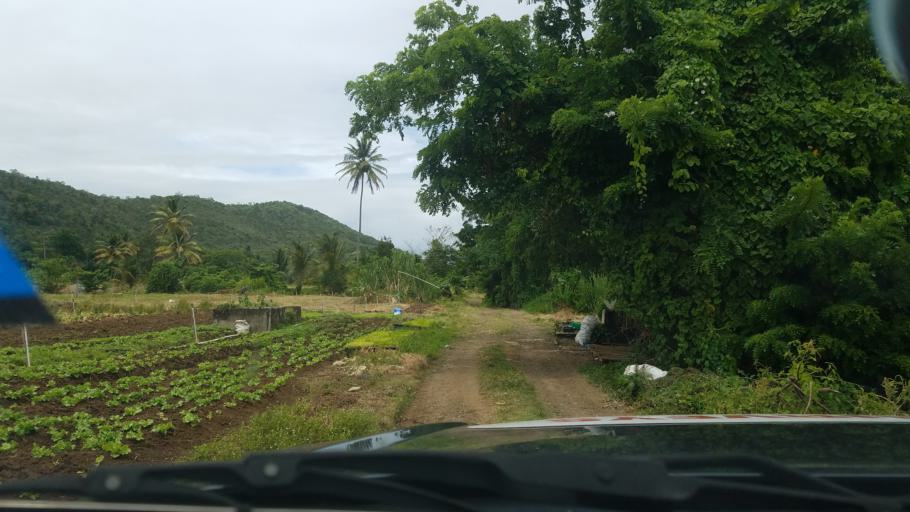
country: LC
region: Gros-Islet
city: Gros Islet
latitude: 14.0281
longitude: -60.9072
